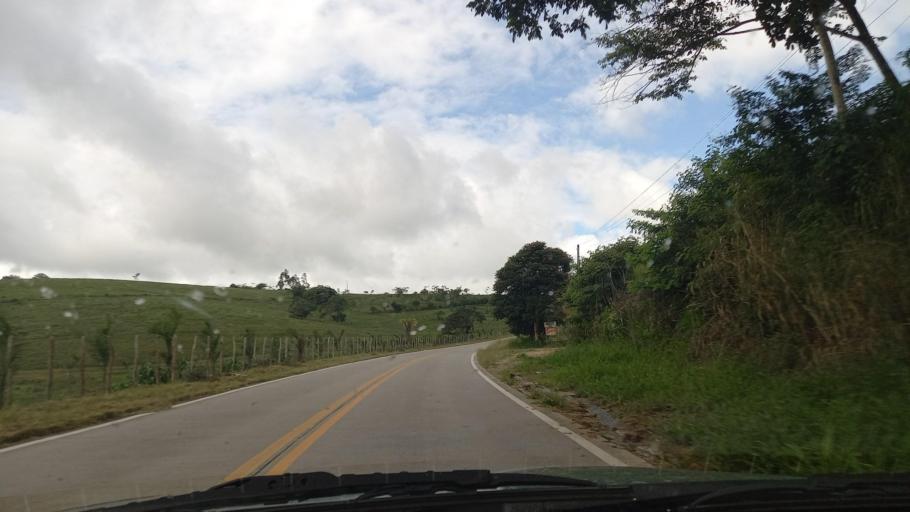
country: BR
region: Pernambuco
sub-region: Quipapa
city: Quipapa
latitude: -8.7874
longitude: -35.9698
